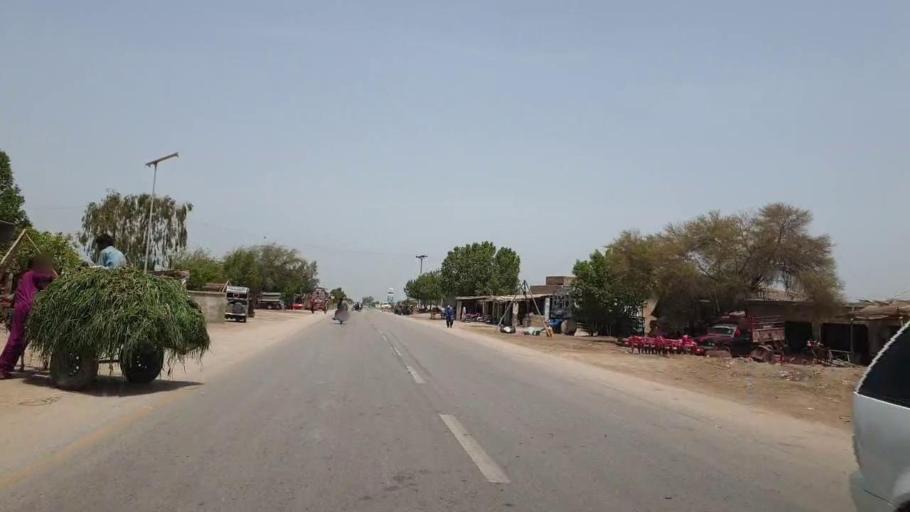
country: PK
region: Sindh
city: Nawabshah
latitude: 26.2221
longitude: 68.4978
